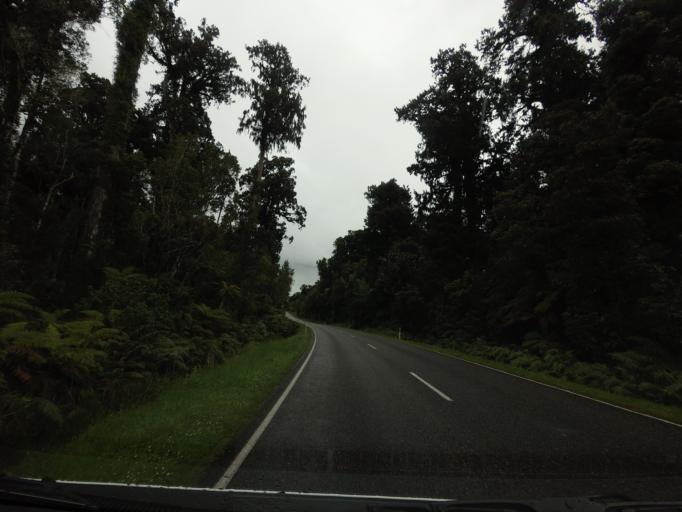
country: NZ
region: West Coast
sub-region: Westland District
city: Hokitika
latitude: -43.0330
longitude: 170.6512
